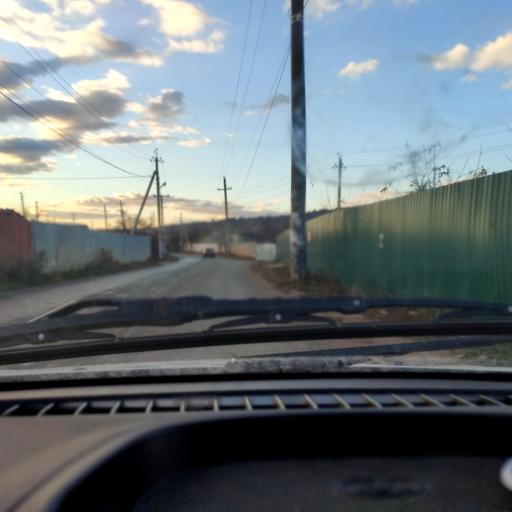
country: RU
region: Samara
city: Povolzhskiy
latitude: 53.4659
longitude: 49.6559
